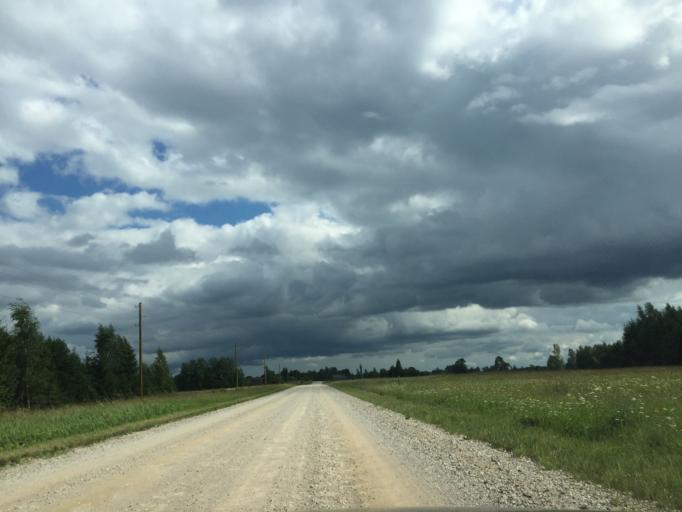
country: LV
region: Malpils
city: Malpils
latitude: 56.8686
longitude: 25.0092
